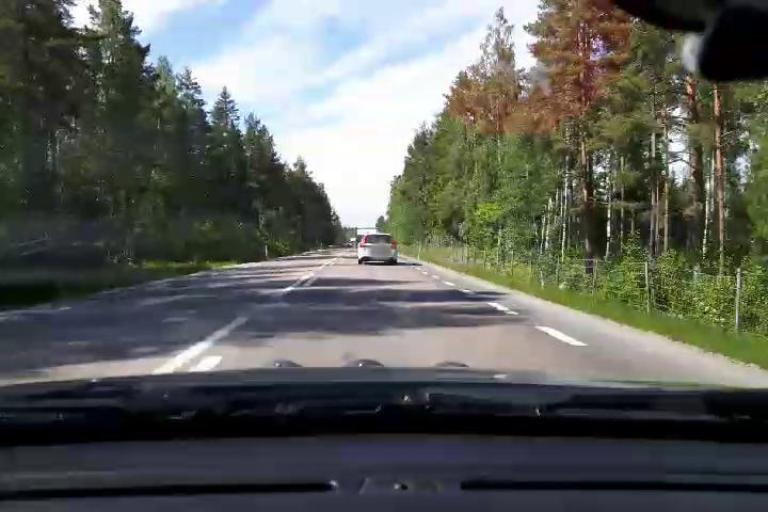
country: SE
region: Gaevleborg
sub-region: Bollnas Kommun
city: Kilafors
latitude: 61.2777
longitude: 16.5235
